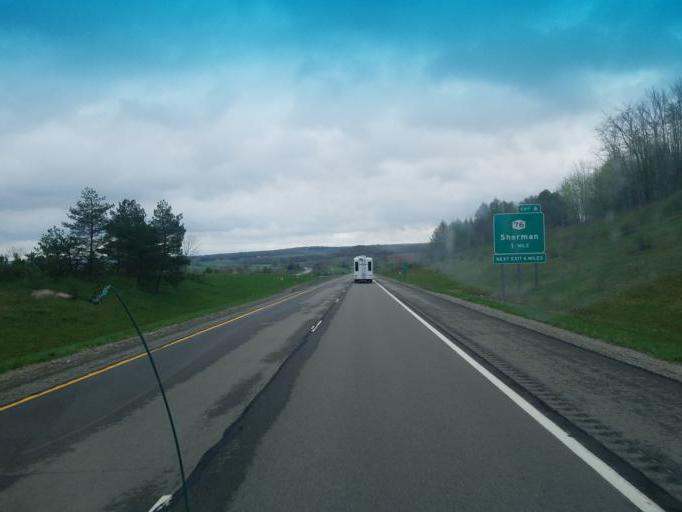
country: US
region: New York
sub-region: Chautauqua County
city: Clymer
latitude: 42.1461
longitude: -79.6214
